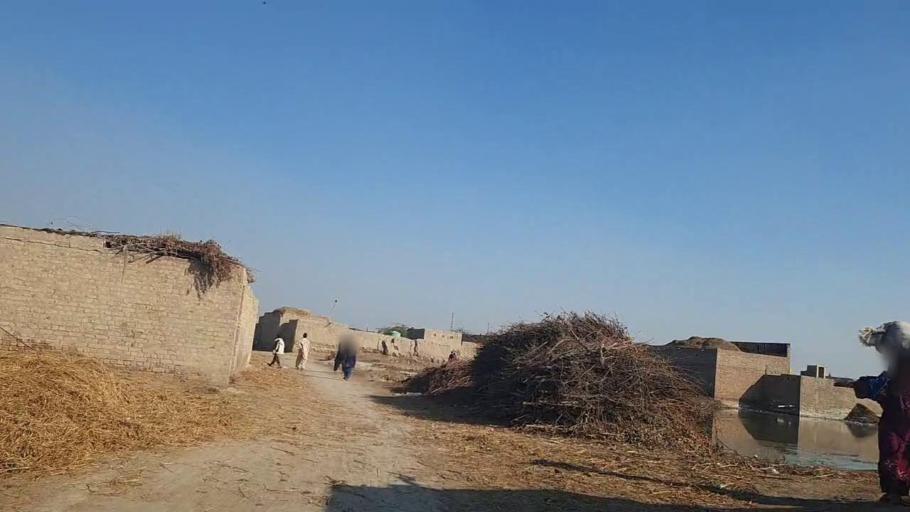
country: PK
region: Sindh
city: Daur
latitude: 26.3177
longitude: 68.1756
